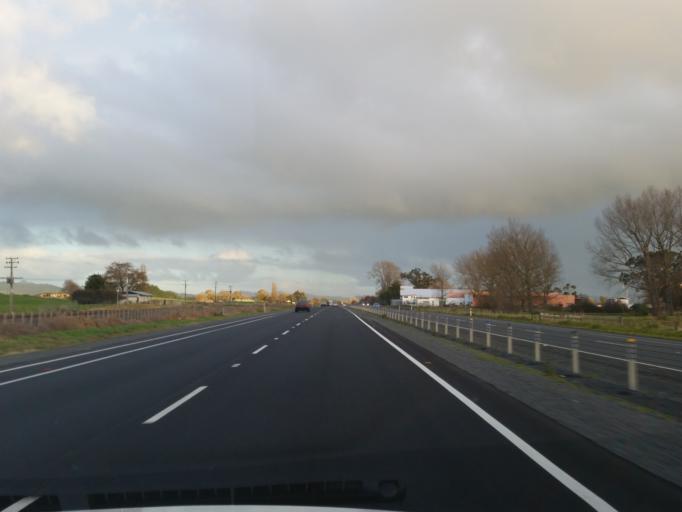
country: NZ
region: Waikato
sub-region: Waikato District
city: Te Kauwhata
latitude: -37.4615
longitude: 175.1562
